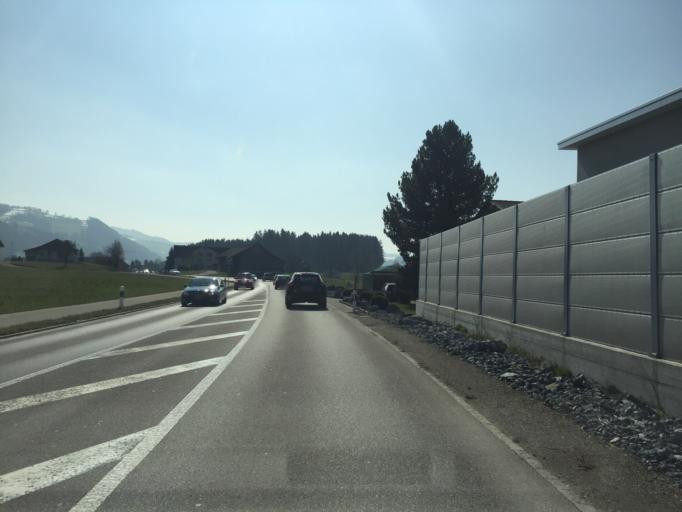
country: CH
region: Saint Gallen
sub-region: Wahlkreis Toggenburg
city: Lutisburg
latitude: 47.3830
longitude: 9.0723
